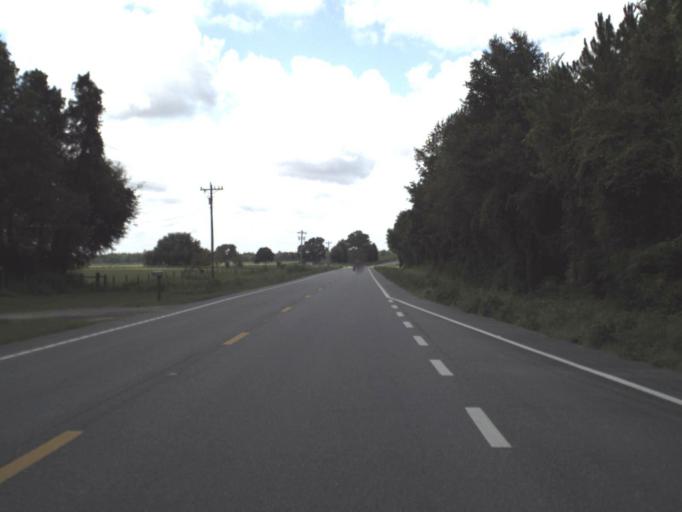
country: US
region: Florida
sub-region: Gilchrist County
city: Trenton
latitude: 29.8690
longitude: -82.8597
